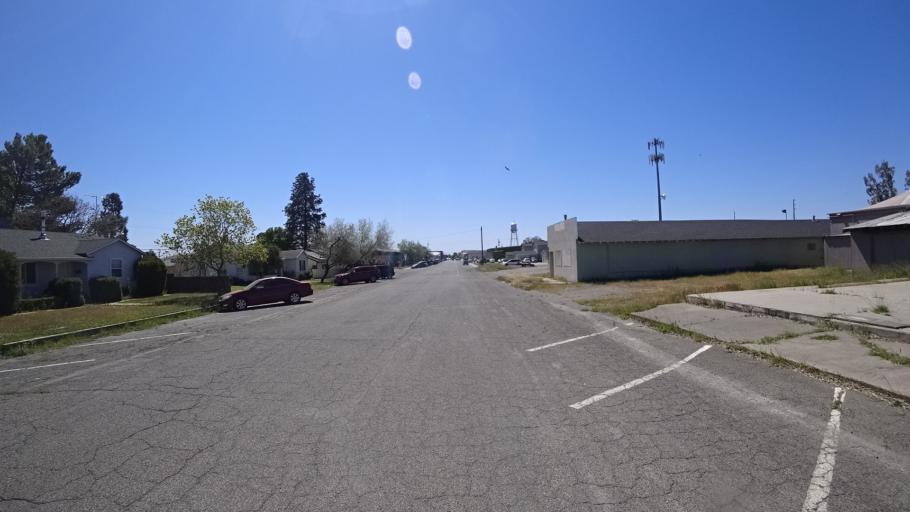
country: US
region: California
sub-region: Glenn County
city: Orland
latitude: 39.7518
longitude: -122.1955
